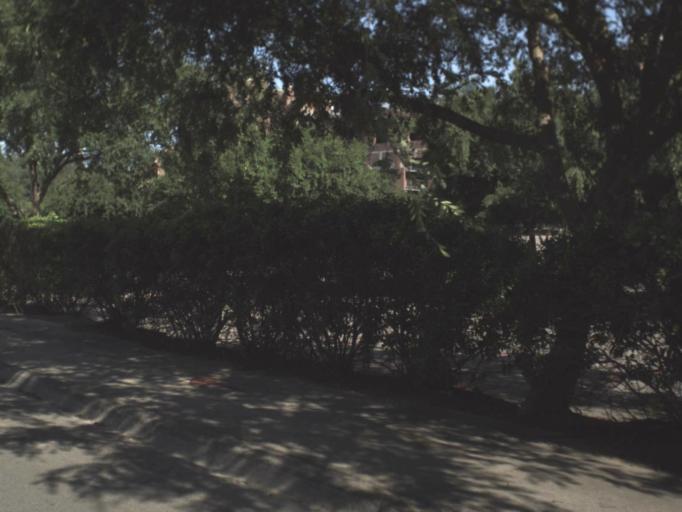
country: US
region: Florida
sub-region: Leon County
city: Tallahassee
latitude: 30.4357
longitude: -84.3024
